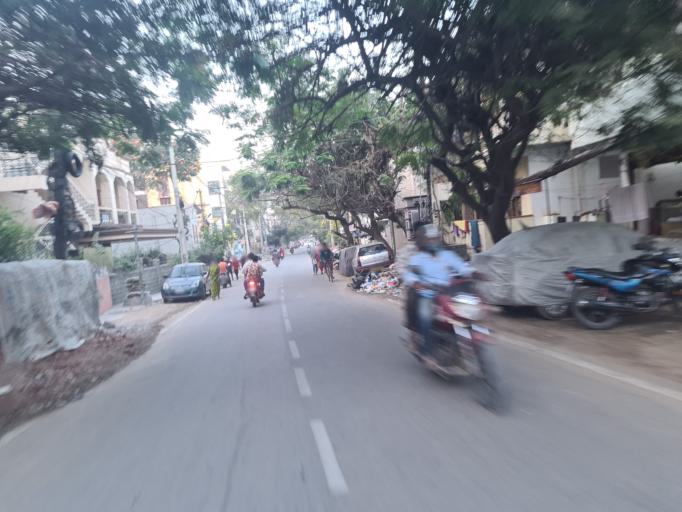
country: IN
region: Telangana
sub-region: Medak
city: Serilingampalle
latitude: 17.4917
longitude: 78.3246
